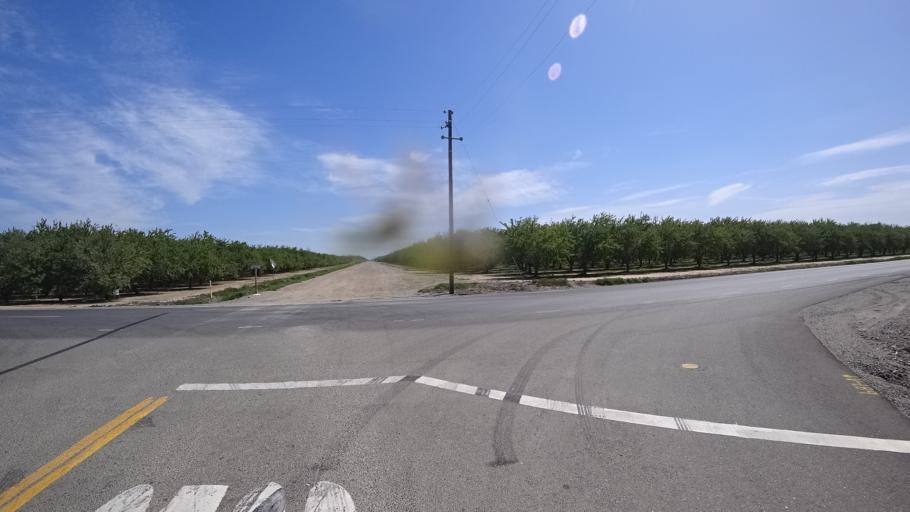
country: US
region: California
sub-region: Glenn County
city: Hamilton City
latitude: 39.6524
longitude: -122.0650
